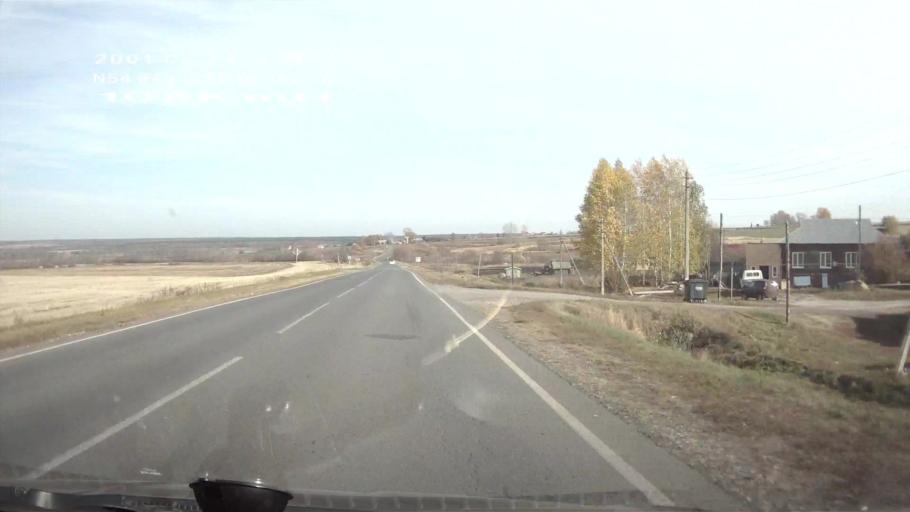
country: RU
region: Mordoviya
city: Turgenevo
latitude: 54.8496
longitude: 46.3813
